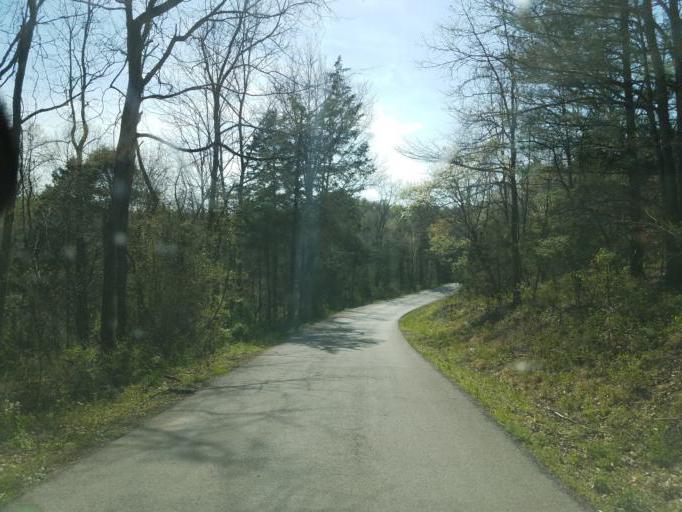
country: US
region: Kentucky
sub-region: Edmonson County
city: Brownsville
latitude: 37.1198
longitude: -86.1321
